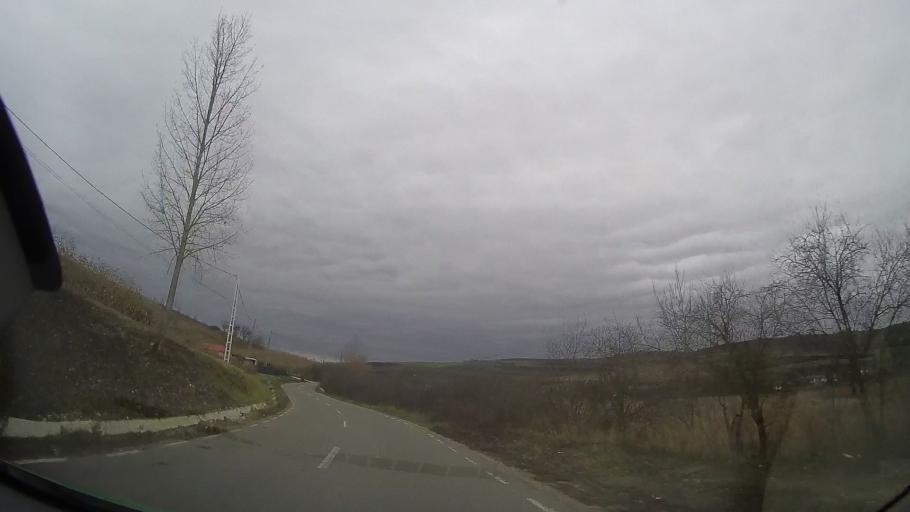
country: RO
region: Cluj
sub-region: Comuna Geaca
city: Geaca
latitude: 46.8366
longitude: 24.1340
